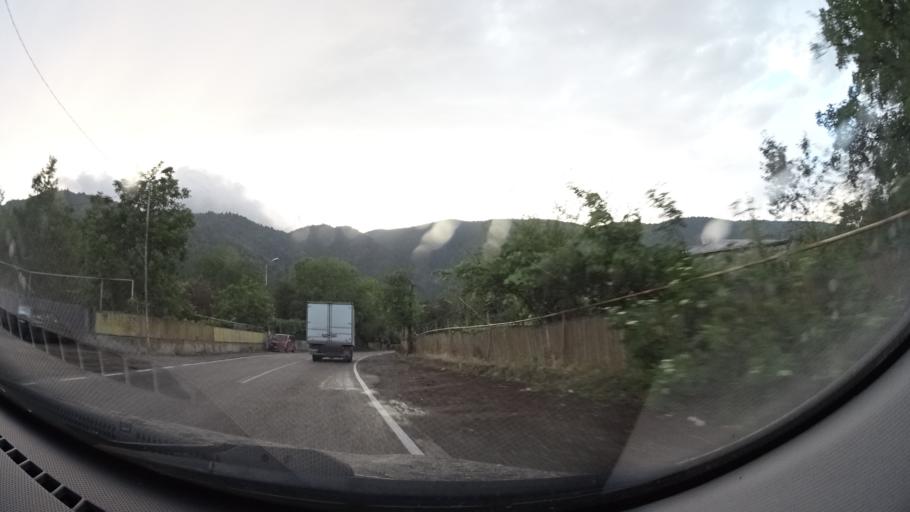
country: GE
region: Samtskhe-Javakheti
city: Borjomi
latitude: 41.9268
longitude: 43.4840
